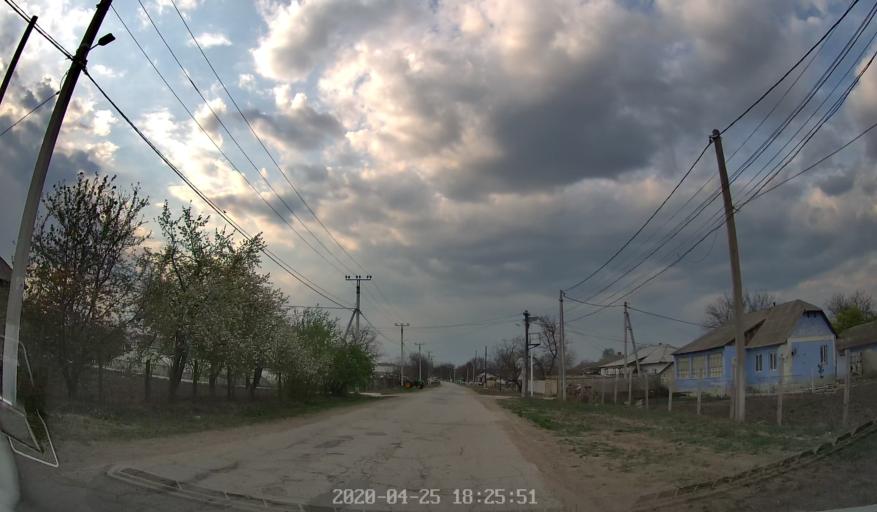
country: MD
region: Criuleni
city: Criuleni
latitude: 47.1637
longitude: 29.1280
